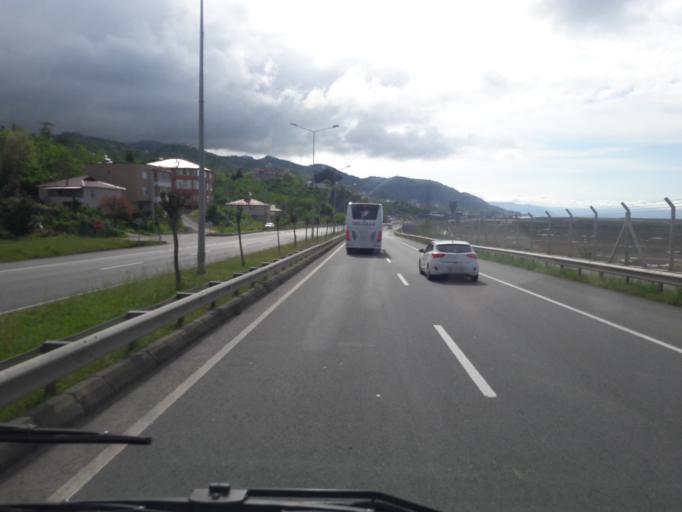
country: TR
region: Giresun
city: Piraziz
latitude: 40.9628
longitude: 38.0938
